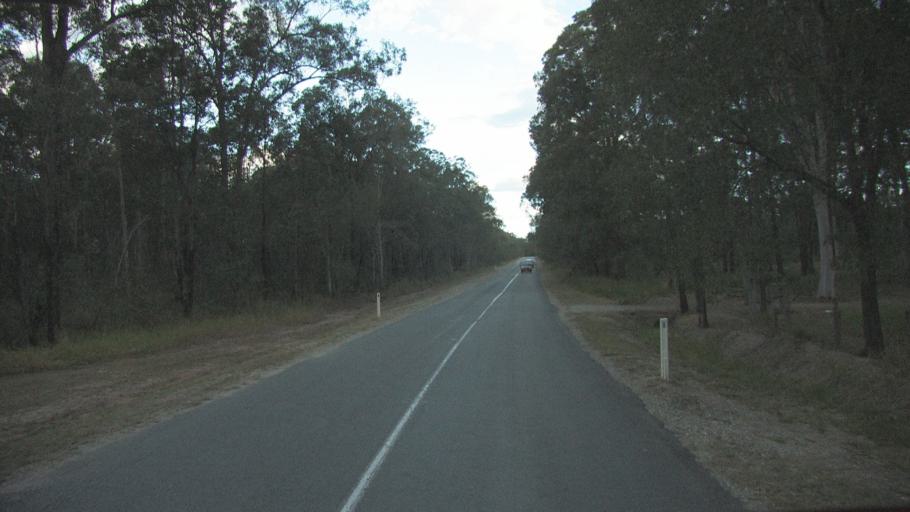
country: AU
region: Queensland
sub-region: Logan
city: Chambers Flat
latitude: -27.7939
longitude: 153.1400
